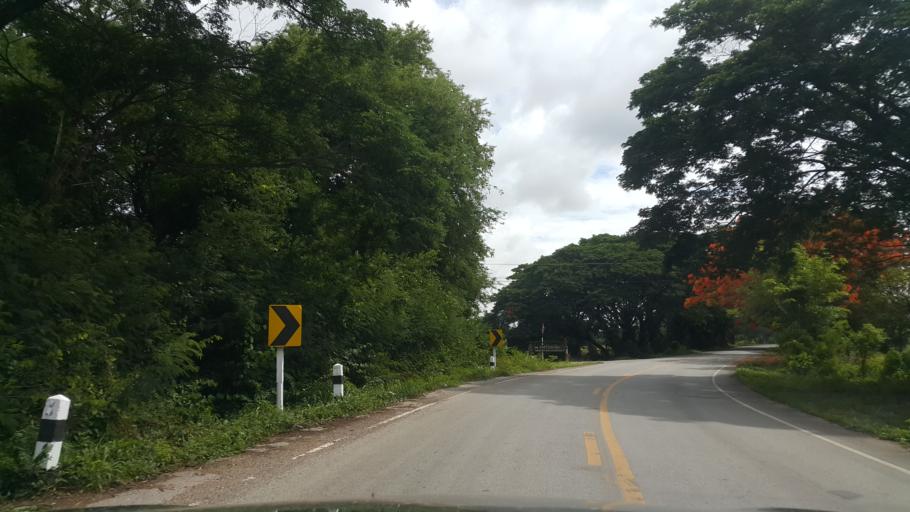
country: TH
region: Uttaradit
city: Thong Saen Khan
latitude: 17.4059
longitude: 100.3190
